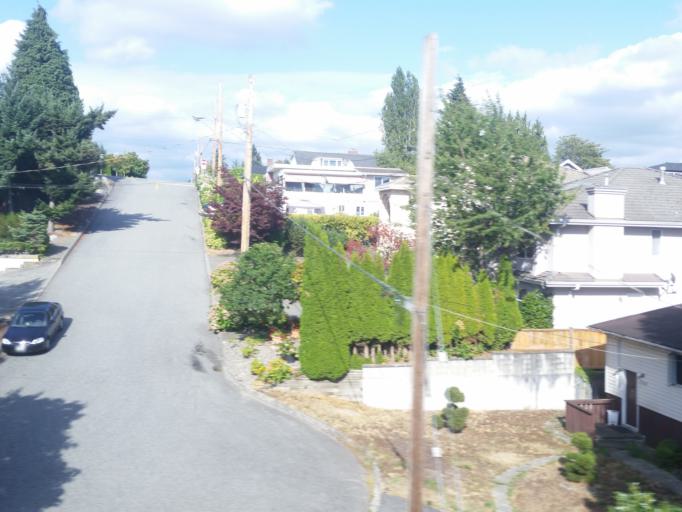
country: CA
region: British Columbia
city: New Westminster
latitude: 49.2016
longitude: -122.9584
